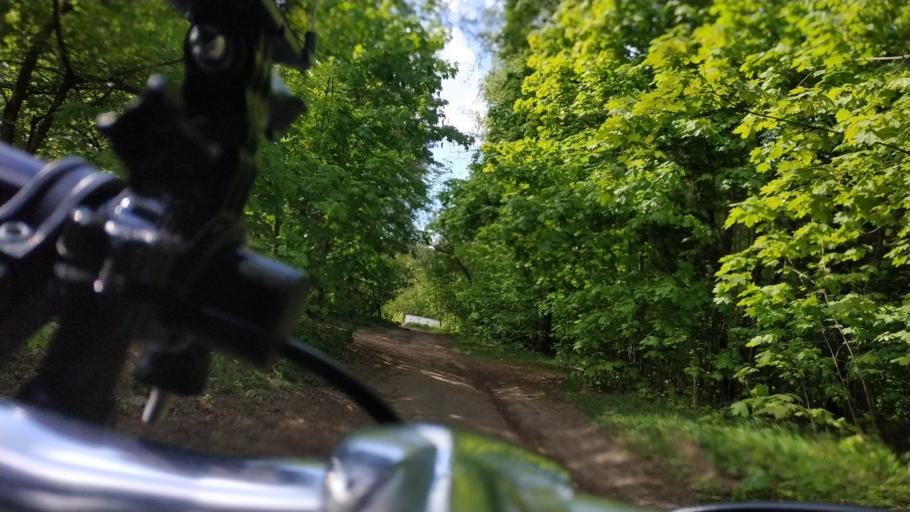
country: RU
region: Moskovskaya
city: Ramenskoye
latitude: 55.5718
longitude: 38.1986
